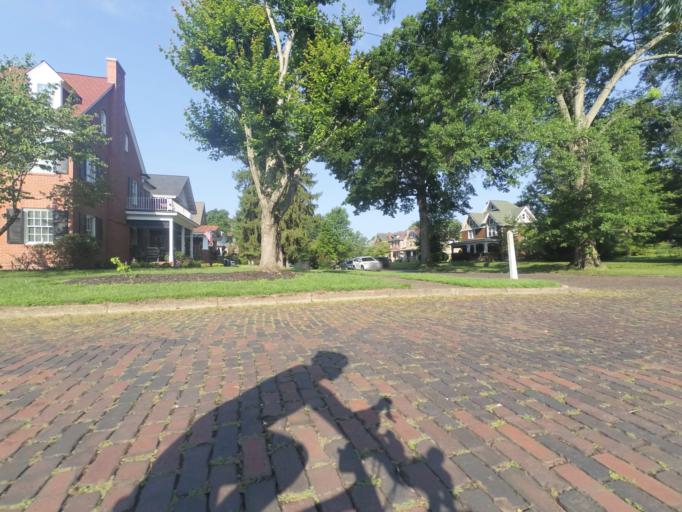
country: US
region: West Virginia
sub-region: Cabell County
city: Huntington
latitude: 38.4073
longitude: -82.4454
